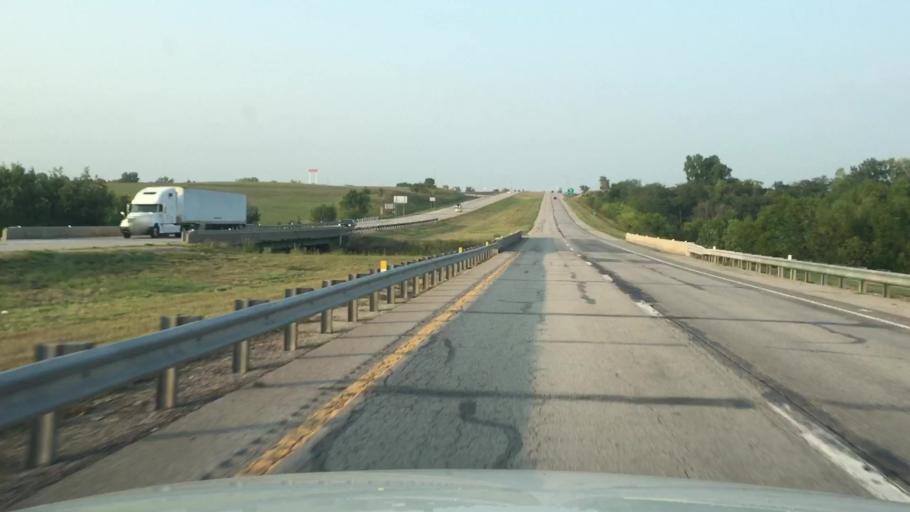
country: US
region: Iowa
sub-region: Decatur County
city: Lamoni
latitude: 40.5674
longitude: -93.9455
